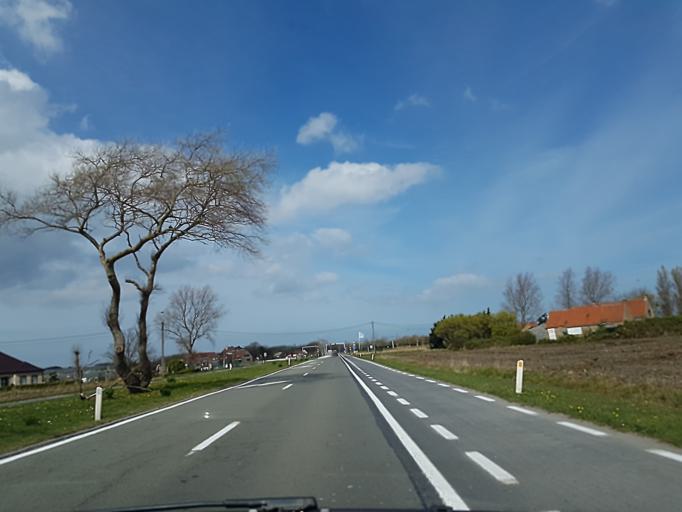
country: BE
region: Flanders
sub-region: Provincie West-Vlaanderen
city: Nieuwpoort
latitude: 51.1514
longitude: 2.7500
